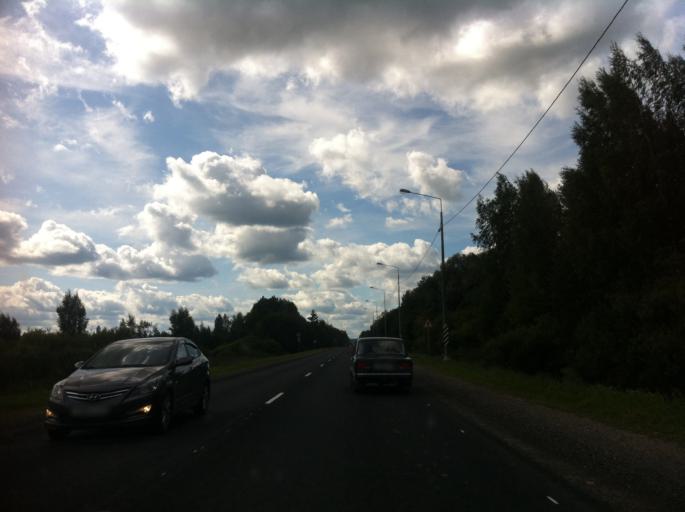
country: RU
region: Pskov
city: Izborsk
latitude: 57.7159
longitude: 27.9164
